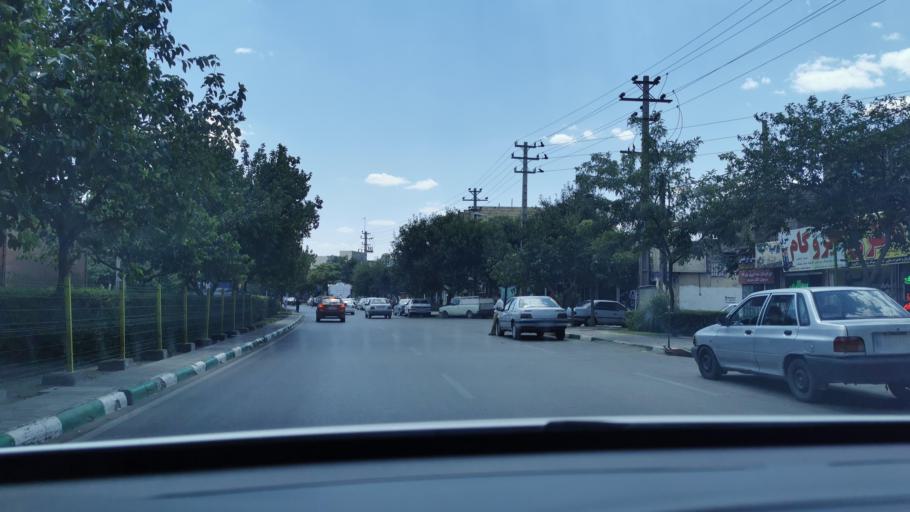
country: IR
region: Razavi Khorasan
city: Mashhad
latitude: 36.3412
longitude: 59.6248
